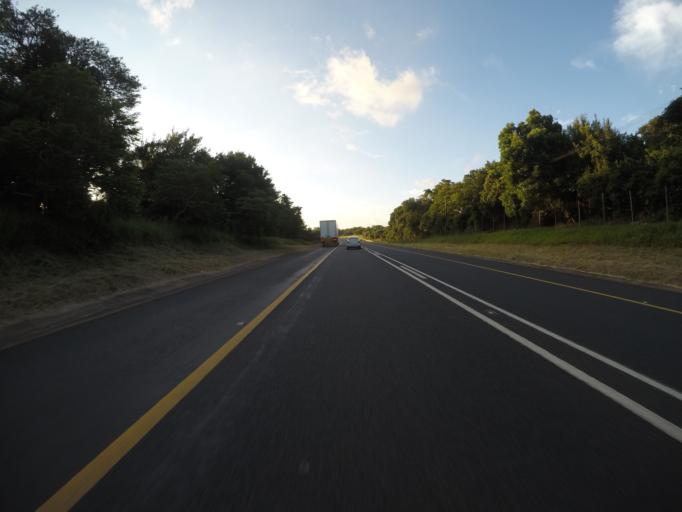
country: ZA
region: KwaZulu-Natal
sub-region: uThungulu District Municipality
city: Richards Bay
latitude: -28.6938
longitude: 32.0080
